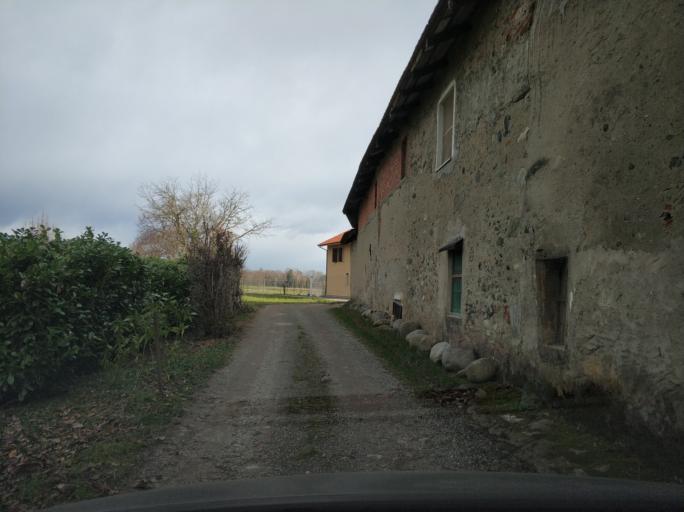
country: IT
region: Piedmont
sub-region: Provincia di Torino
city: Robassomero
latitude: 45.2179
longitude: 7.5744
